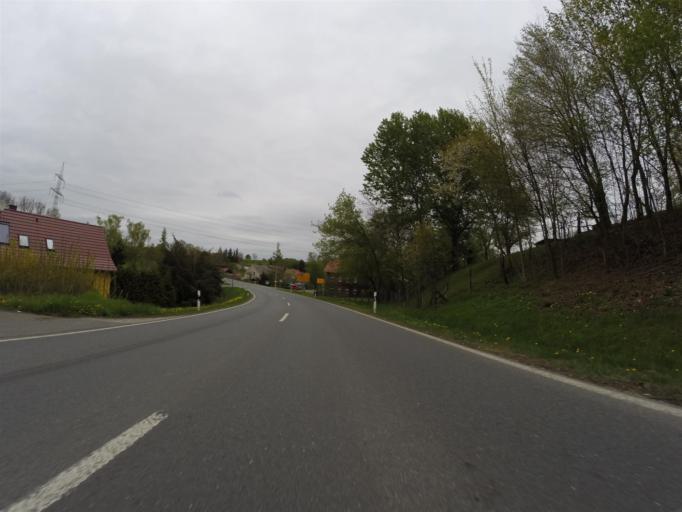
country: DE
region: Thuringia
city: Camburg
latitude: 51.0620
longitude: 11.7222
